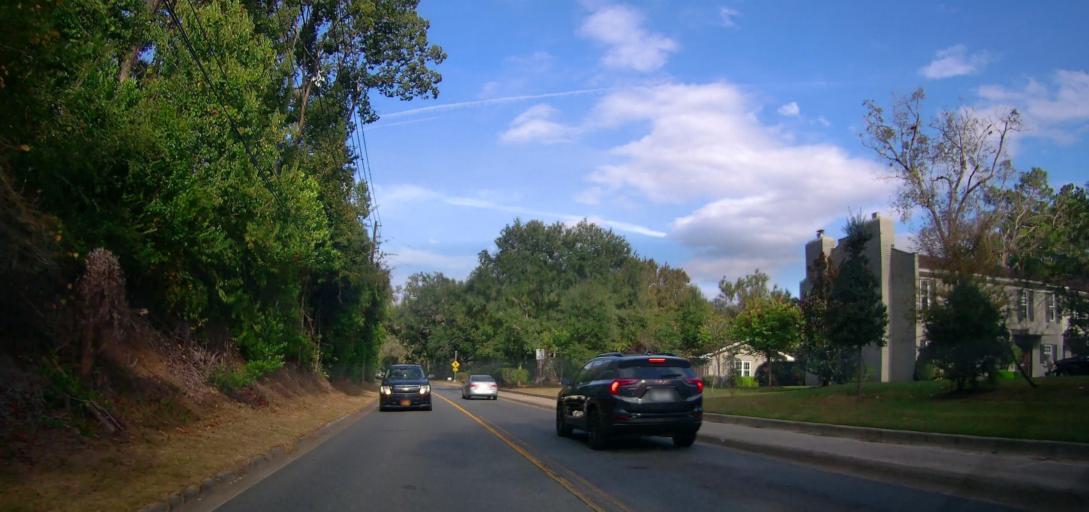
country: US
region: Florida
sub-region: Leon County
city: Tallahassee
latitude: 30.4666
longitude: -84.2533
